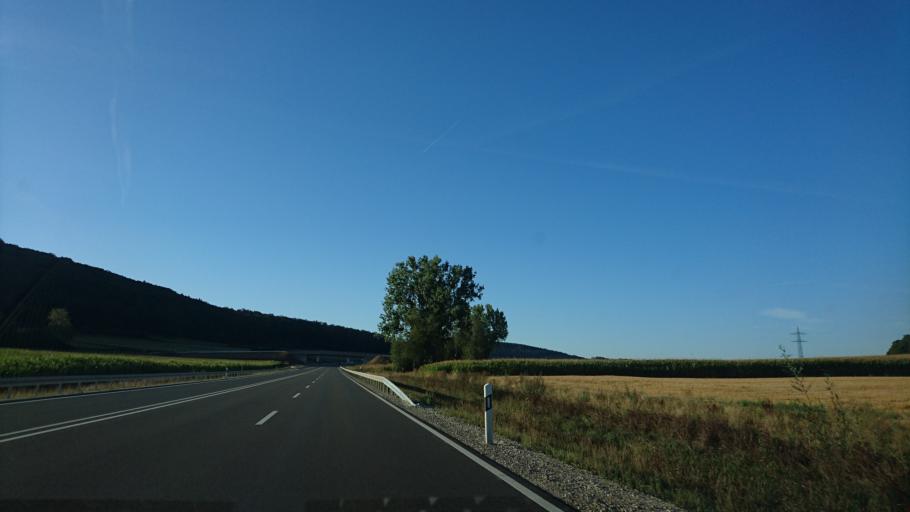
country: DE
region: Bavaria
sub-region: Regierungsbezirk Mittelfranken
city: Treuchtlingen
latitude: 48.9813
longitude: 10.9423
